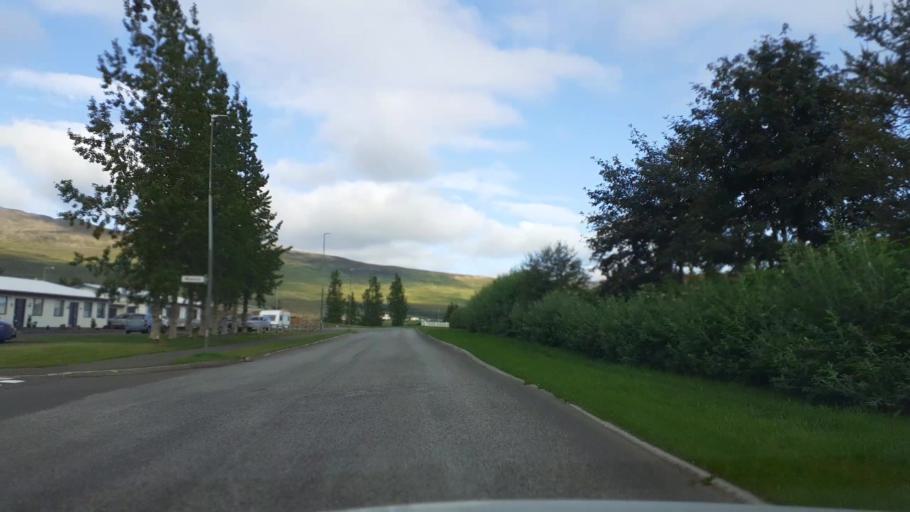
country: IS
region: Northeast
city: Akureyri
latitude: 65.6959
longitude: -18.1407
